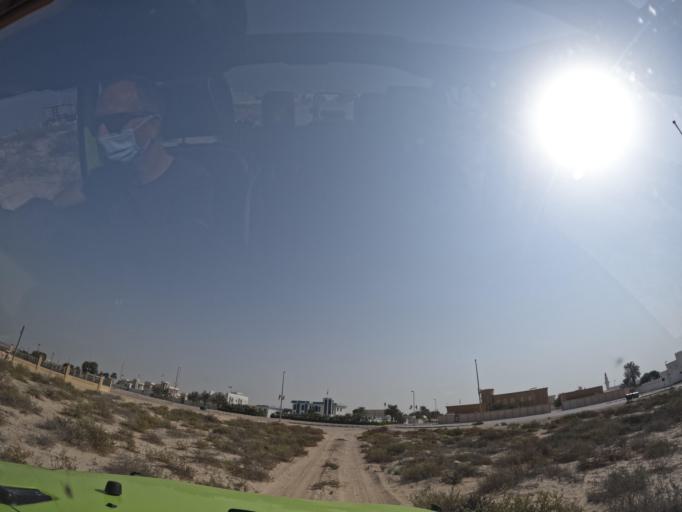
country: AE
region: Umm al Qaywayn
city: Umm al Qaywayn
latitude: 25.4786
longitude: 55.5304
